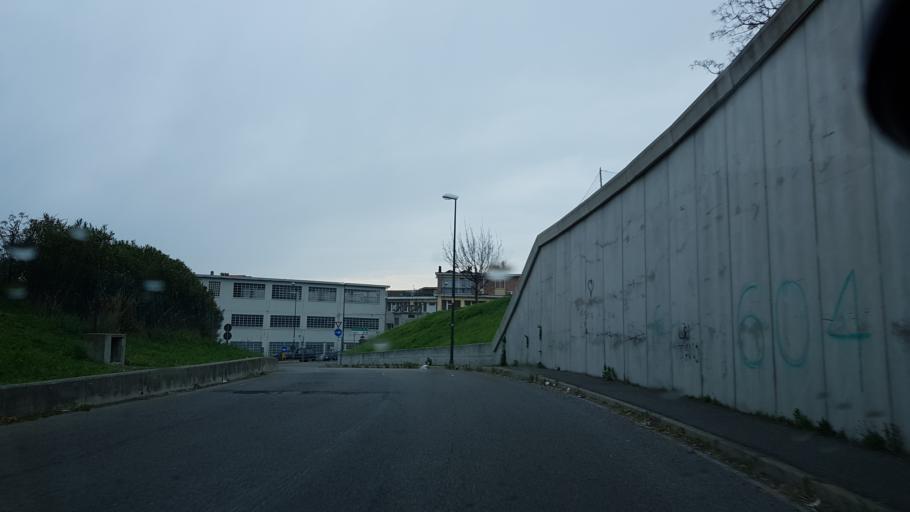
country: IT
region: Liguria
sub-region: Provincia di Savona
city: Savona
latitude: 44.2993
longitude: 8.4580
